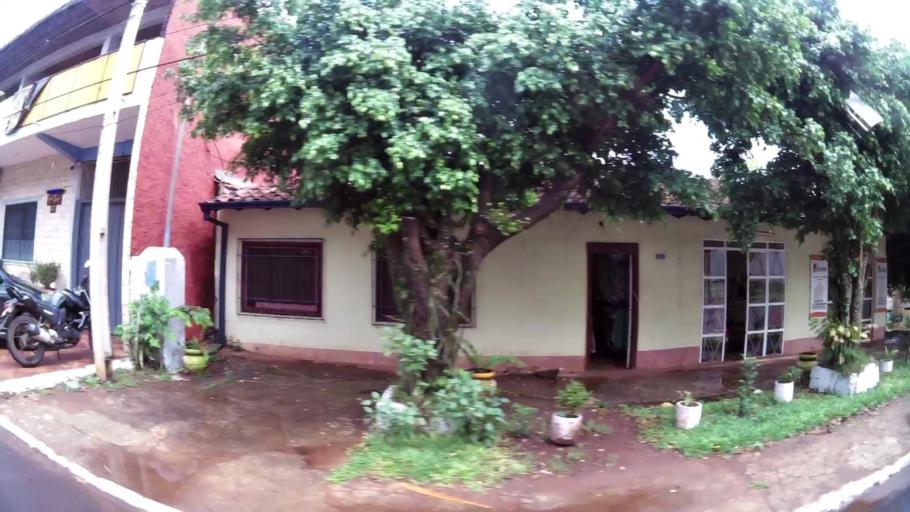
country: PY
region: Alto Parana
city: Ciudad del Este
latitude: -25.5131
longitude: -54.6448
